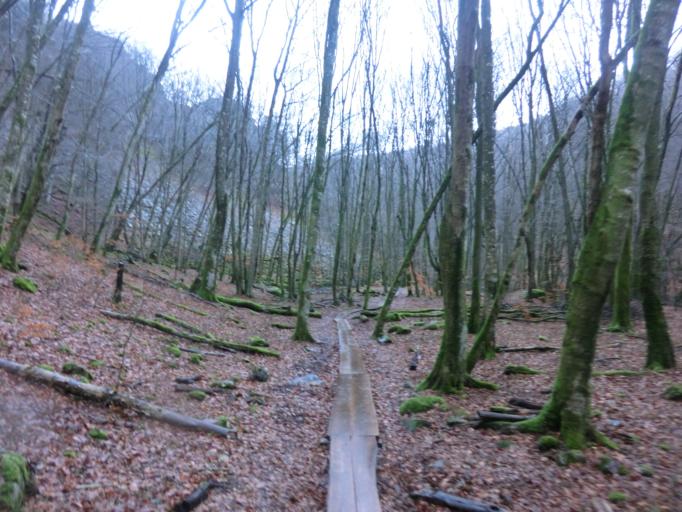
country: SE
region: Skane
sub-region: Klippans Kommun
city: Ljungbyhed
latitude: 56.0307
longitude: 13.2367
